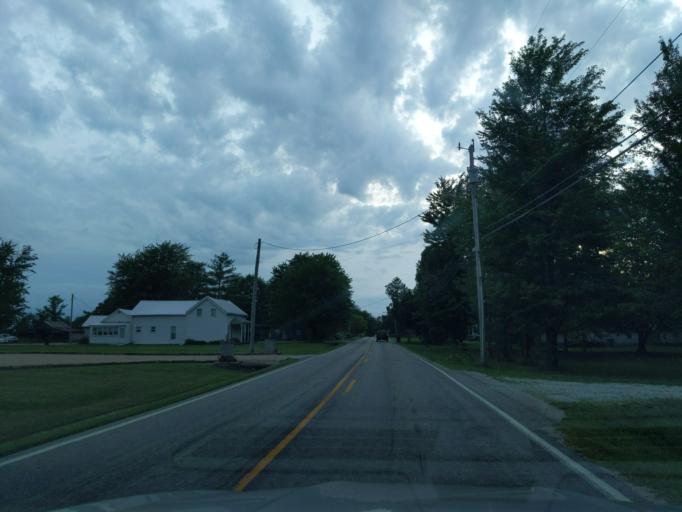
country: US
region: Indiana
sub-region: Ripley County
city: Osgood
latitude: 39.2049
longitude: -85.3218
